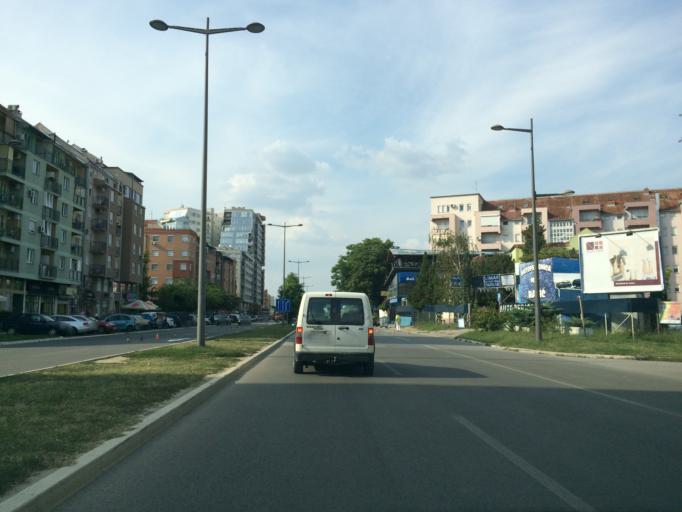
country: RS
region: Autonomna Pokrajina Vojvodina
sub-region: Juznobacki Okrug
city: Novi Sad
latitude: 45.2410
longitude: 19.8219
